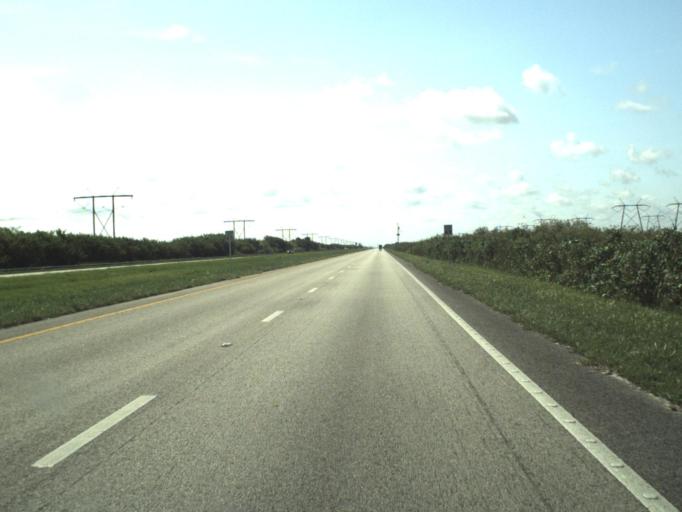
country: US
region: Florida
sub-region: Broward County
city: Weston
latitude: 26.2850
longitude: -80.4996
